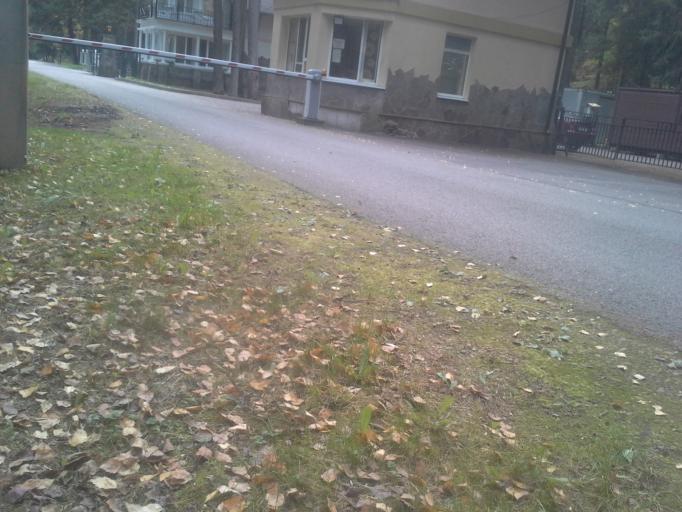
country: RU
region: Moskovskaya
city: Selyatino
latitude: 55.4710
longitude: 36.9704
